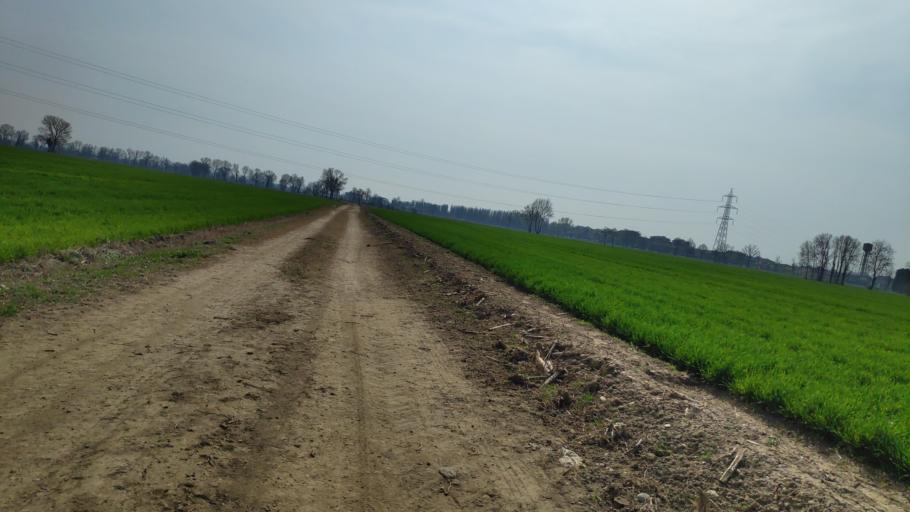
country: IT
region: Lombardy
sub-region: Citta metropolitana di Milano
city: Pantigliate
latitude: 45.4476
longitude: 9.3611
